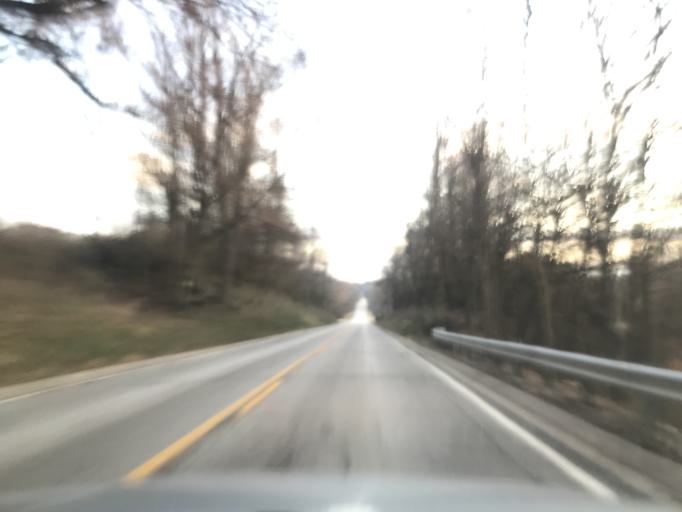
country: US
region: Illinois
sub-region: Henderson County
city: Oquawka
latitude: 40.9116
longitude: -90.8643
